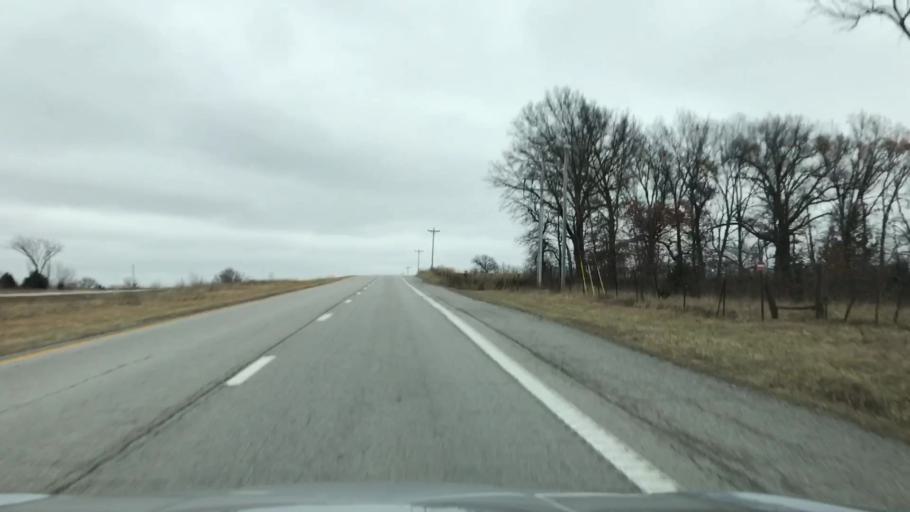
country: US
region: Missouri
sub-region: Linn County
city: Linneus
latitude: 39.7779
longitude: -93.2034
